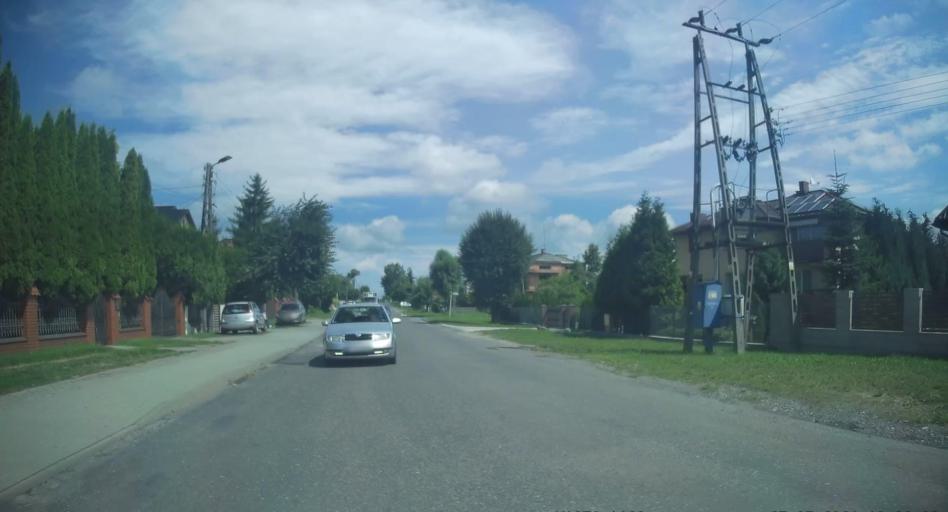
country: PL
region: Lodz Voivodeship
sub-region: Powiat rawski
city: Rawa Mazowiecka
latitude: 51.7478
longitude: 20.2388
